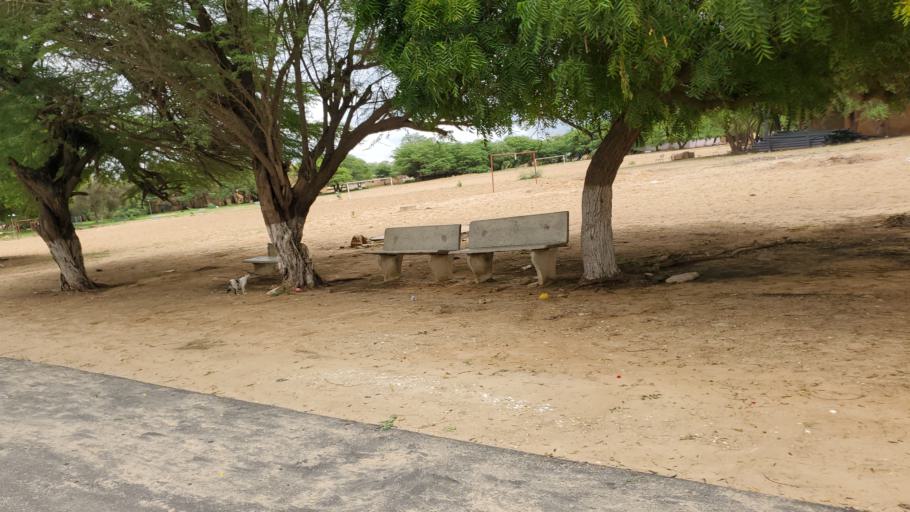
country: SN
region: Saint-Louis
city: Saint-Louis
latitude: 16.0665
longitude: -16.4261
